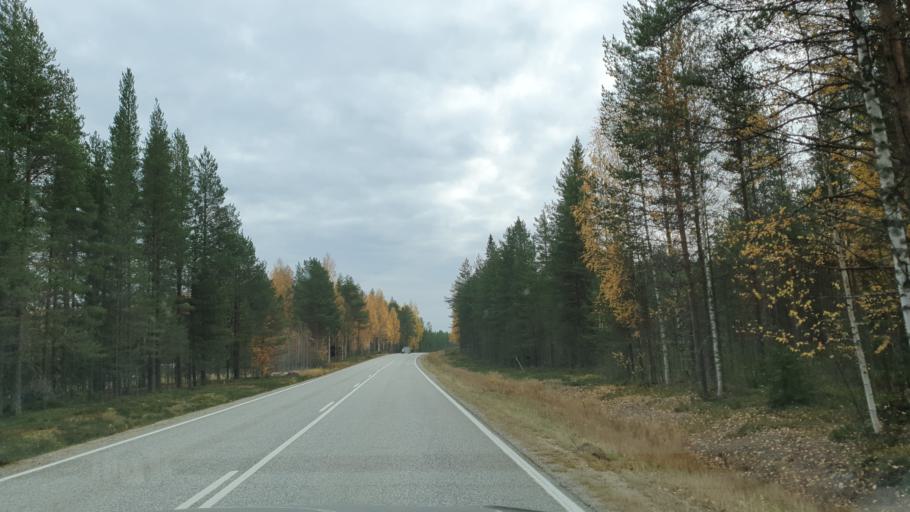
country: FI
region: Kainuu
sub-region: Kehys-Kainuu
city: Puolanka
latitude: 65.2383
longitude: 27.5875
